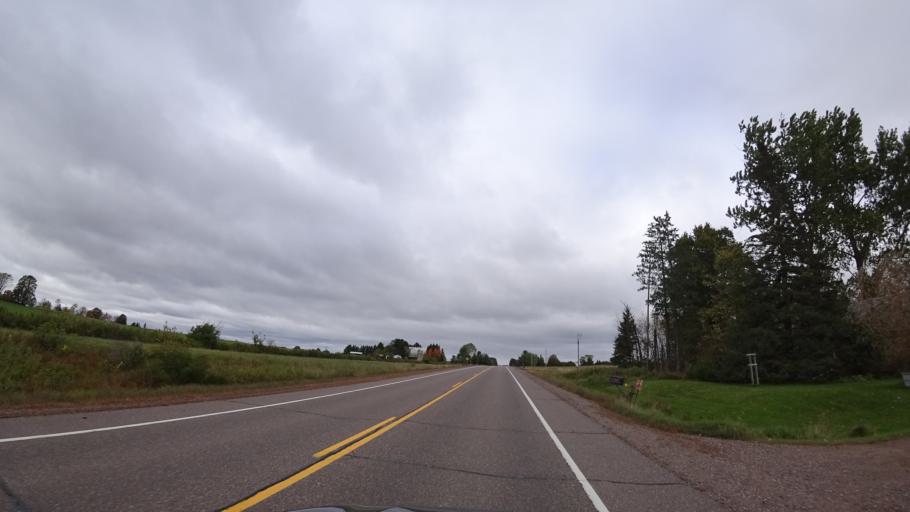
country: US
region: Wisconsin
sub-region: Rusk County
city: Ladysmith
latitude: 45.5339
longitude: -91.1115
